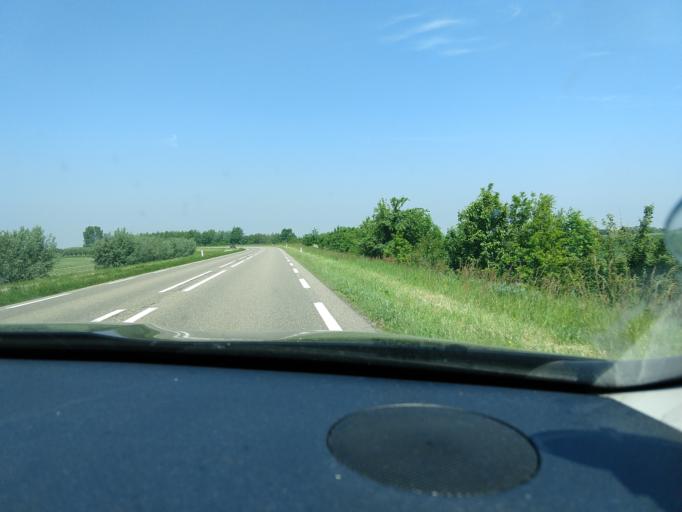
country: NL
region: Zeeland
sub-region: Gemeente Tholen
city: Tholen
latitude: 51.5446
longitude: 4.1314
